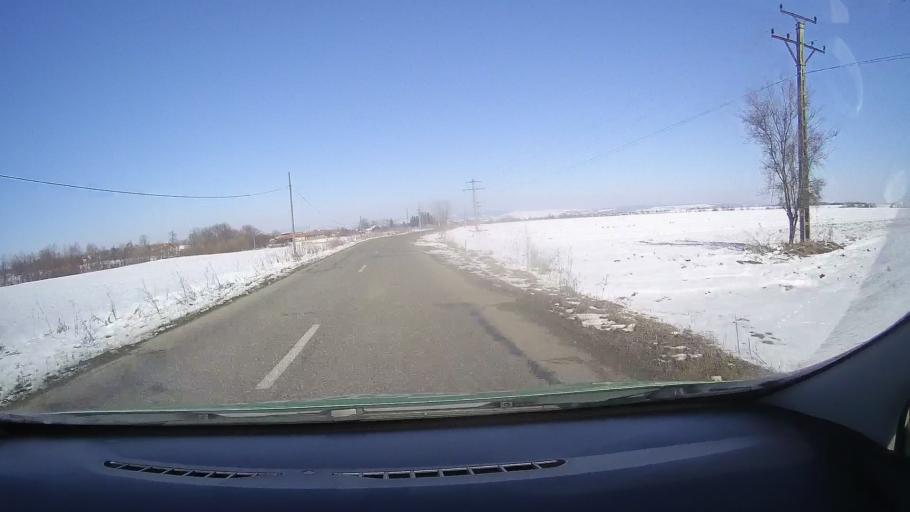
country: RO
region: Brasov
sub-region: Comuna Harseni
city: Harseni
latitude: 45.7776
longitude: 25.0010
